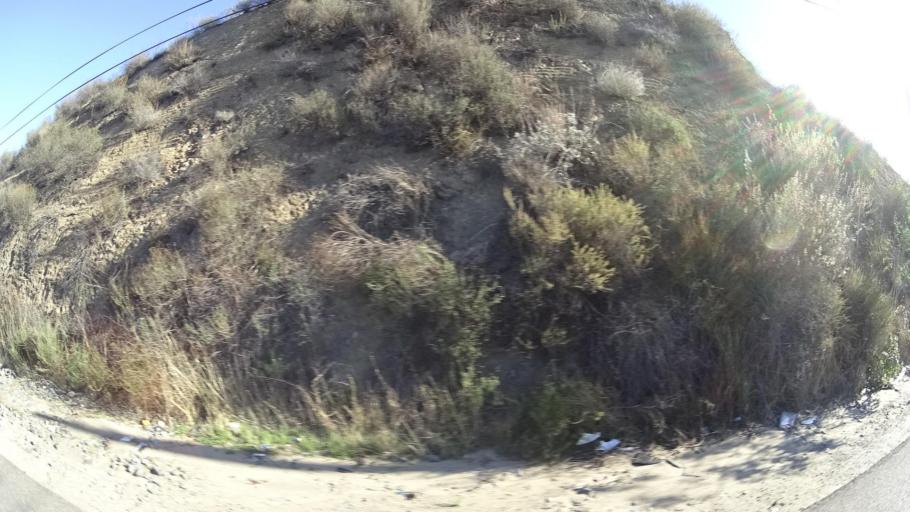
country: US
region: California
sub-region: San Diego County
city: Jamul
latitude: 32.6411
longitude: -116.7729
